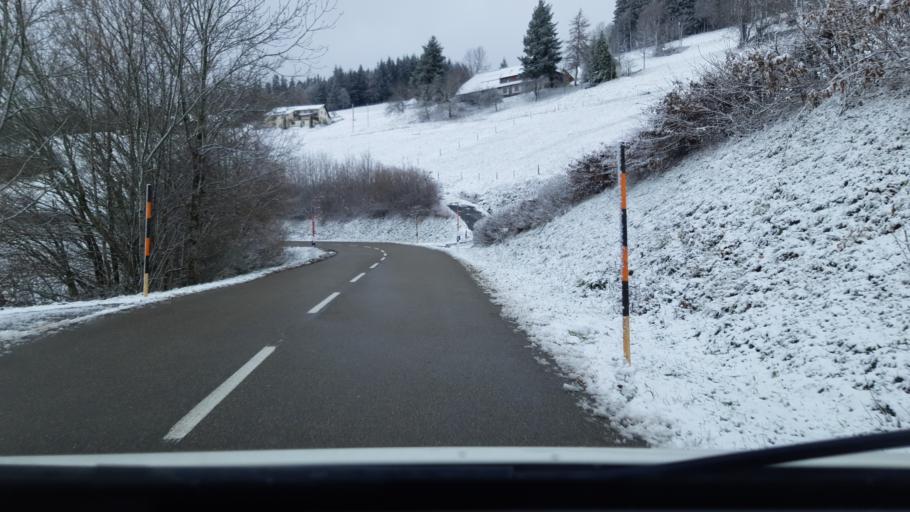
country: DE
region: Baden-Wuerttemberg
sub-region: Freiburg Region
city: Horben
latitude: 47.9183
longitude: 7.8471
